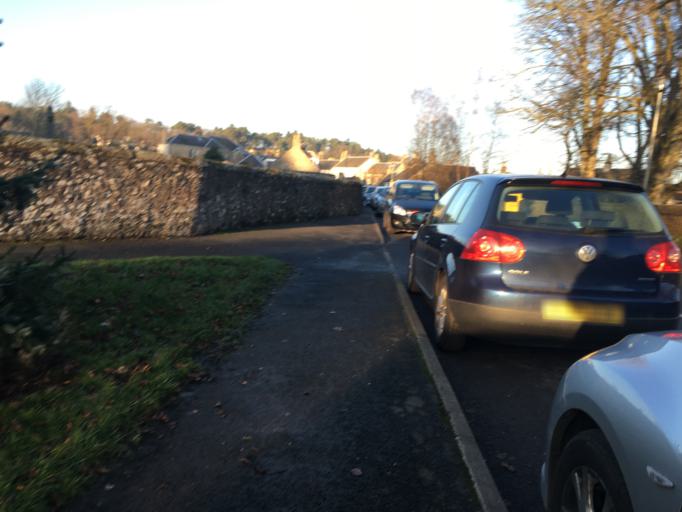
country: GB
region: Scotland
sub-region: The Scottish Borders
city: West Linton
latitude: 55.7503
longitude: -3.3561
